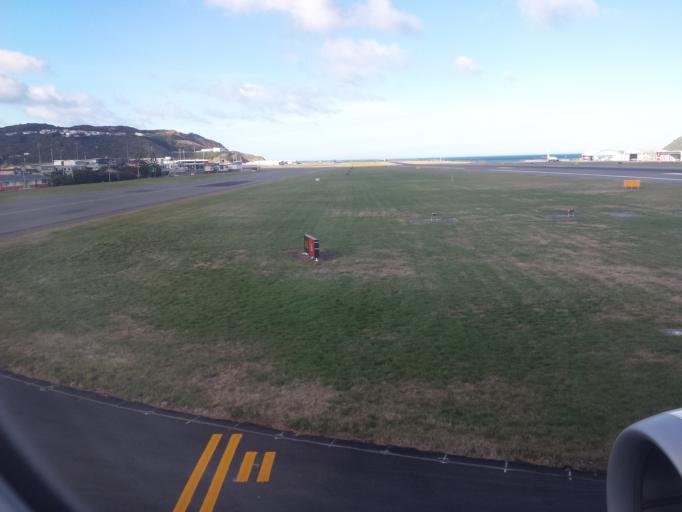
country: NZ
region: Wellington
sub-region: Wellington City
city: Wellington
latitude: -41.3217
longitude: 174.8082
